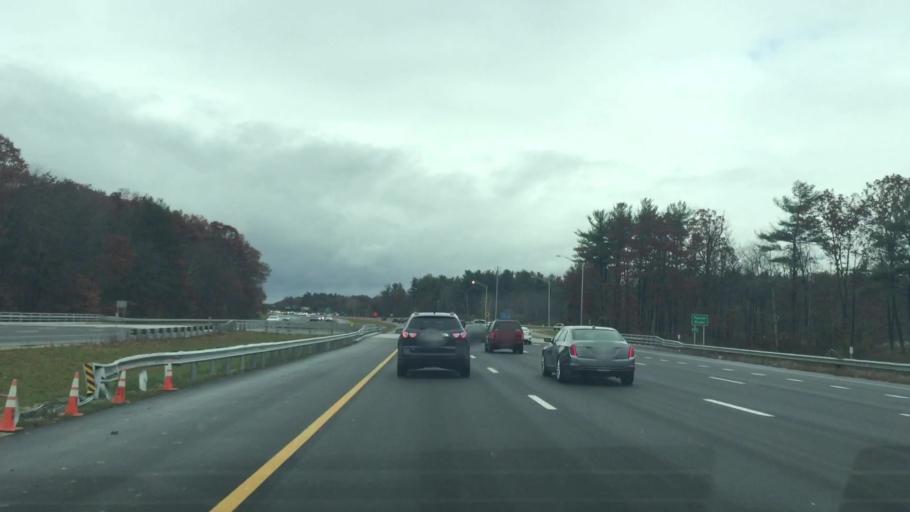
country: US
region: New Hampshire
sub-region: Rockingham County
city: Hampton Falls
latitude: 42.9330
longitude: -70.8631
